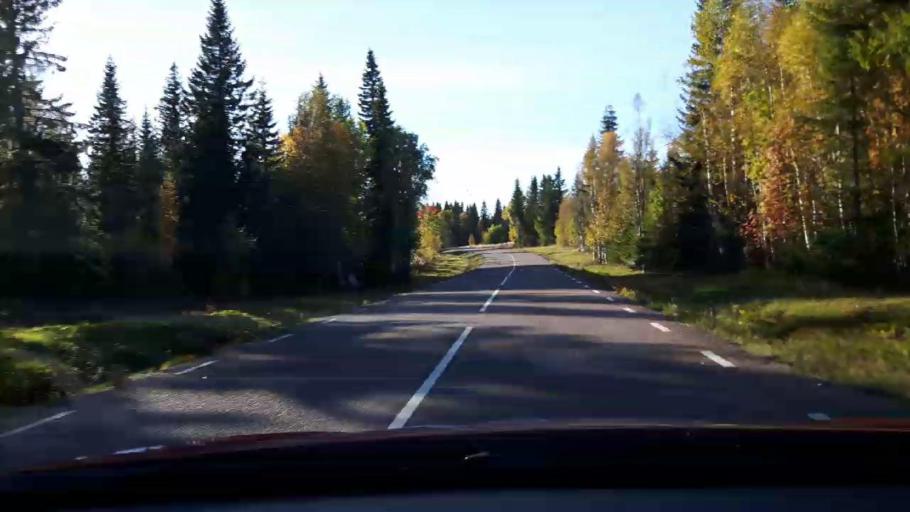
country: SE
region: Jaemtland
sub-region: Stroemsunds Kommun
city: Stroemsund
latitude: 63.8653
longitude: 15.1421
